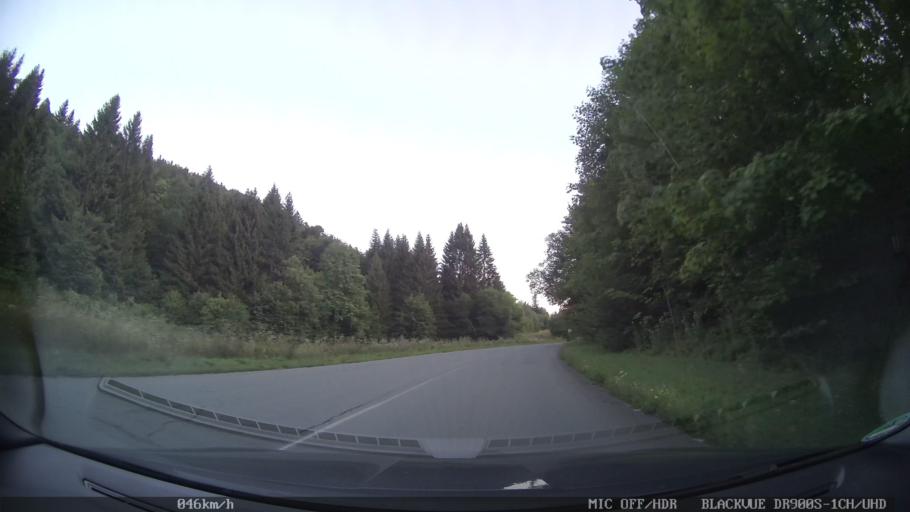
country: HR
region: Primorsko-Goranska
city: Vrbovsko
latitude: 45.2101
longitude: 15.0298
